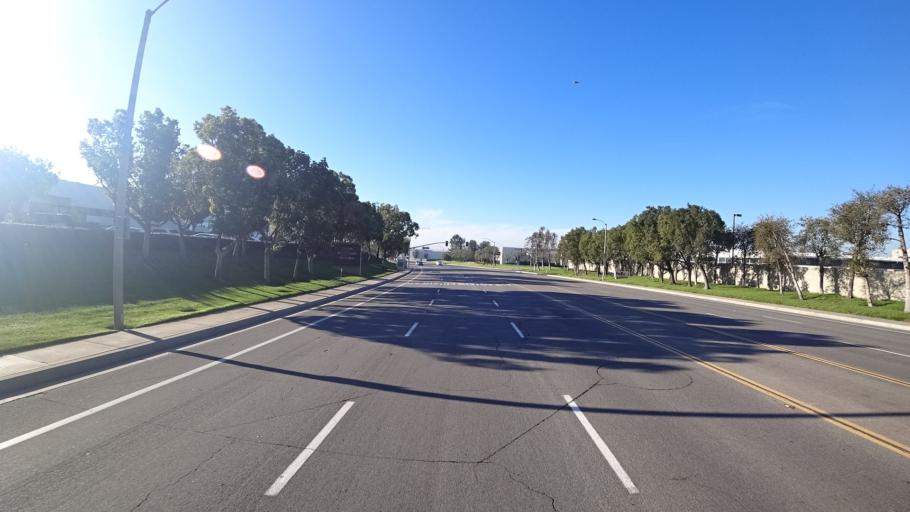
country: US
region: California
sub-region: Orange County
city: Lake Forest
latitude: 33.6616
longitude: -117.7092
